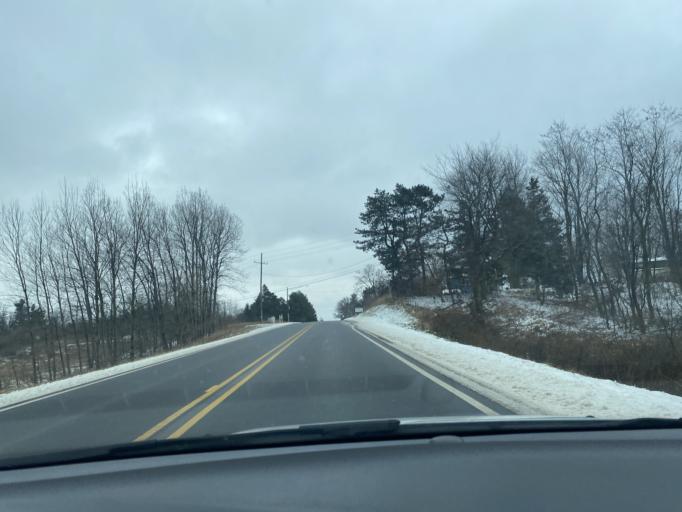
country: US
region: Michigan
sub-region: Lapeer County
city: North Branch
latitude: 43.2073
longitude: -83.2069
